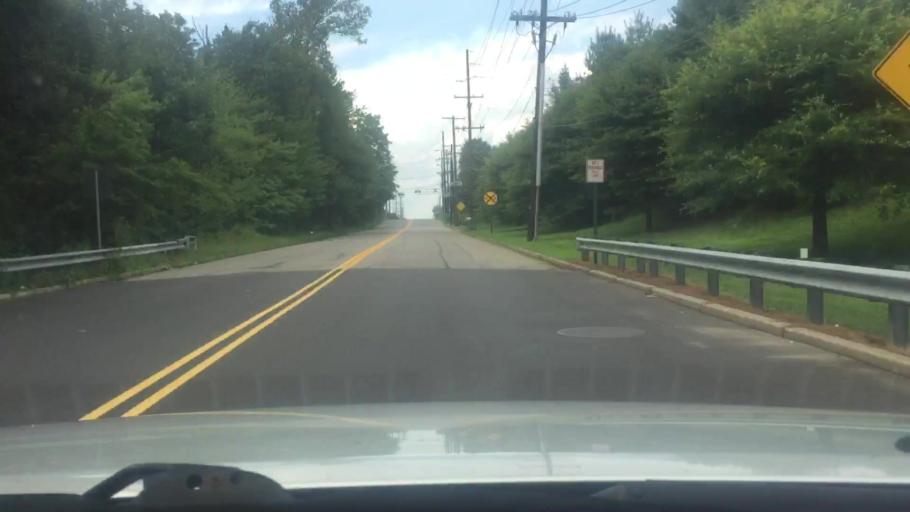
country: US
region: New Jersey
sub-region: Middlesex County
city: East Brunswick
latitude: 40.4417
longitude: -74.4075
